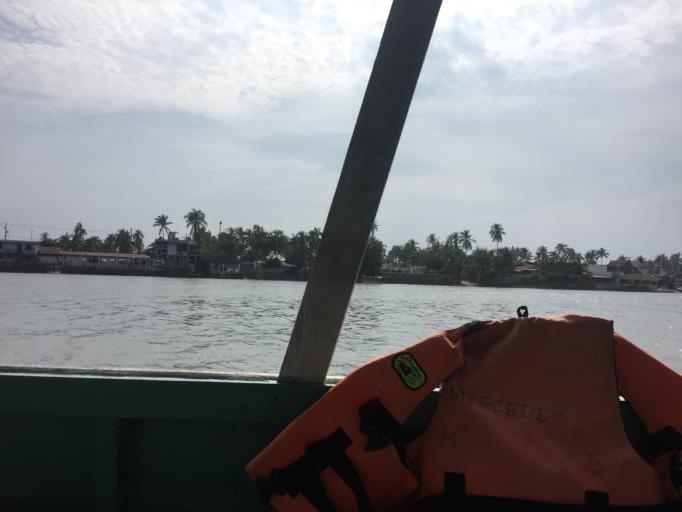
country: MX
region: Guerrero
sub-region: Coyuca de Benitez
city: Colonia Luces en el Mar
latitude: 16.9023
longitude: -99.9690
